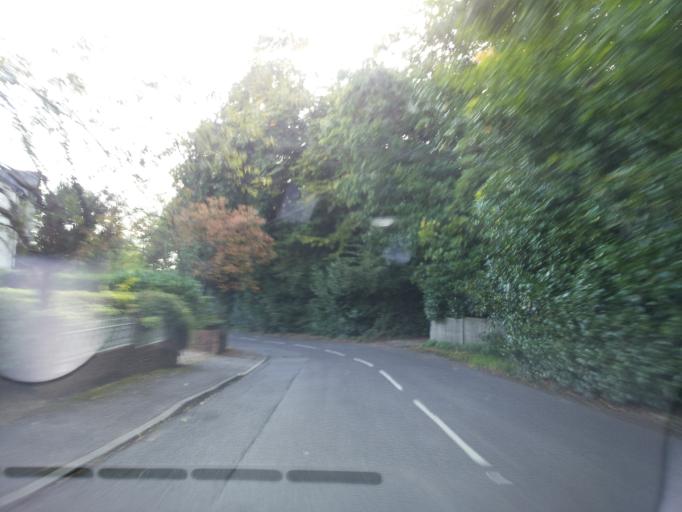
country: GB
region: England
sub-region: Surrey
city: Windlesham
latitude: 51.3664
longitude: -0.6582
